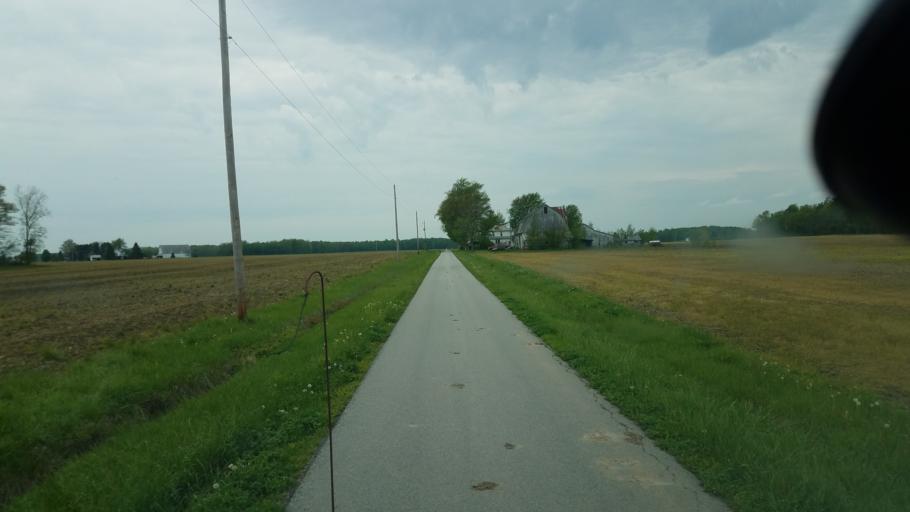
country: US
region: Ohio
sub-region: Huron County
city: Willard
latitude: 41.0190
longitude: -82.8522
